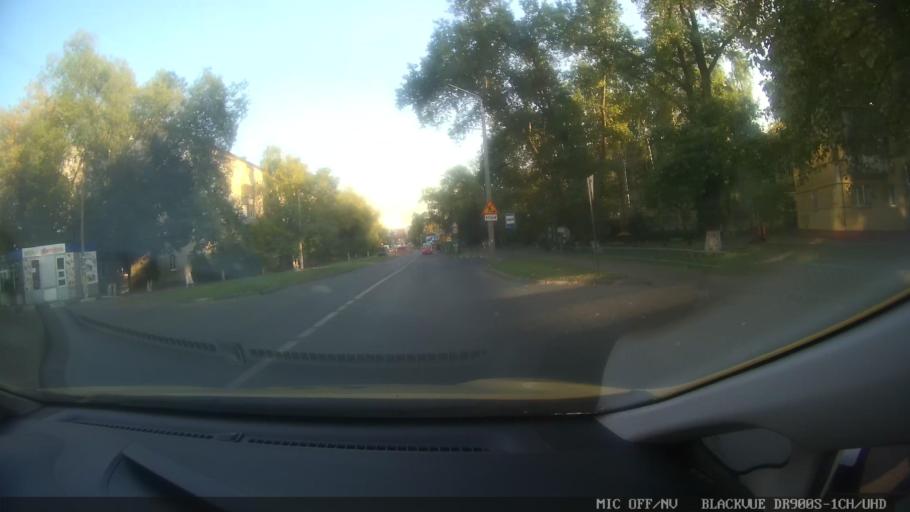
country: RU
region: Moscow
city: Nekrasovka
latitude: 55.6994
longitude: 37.8982
